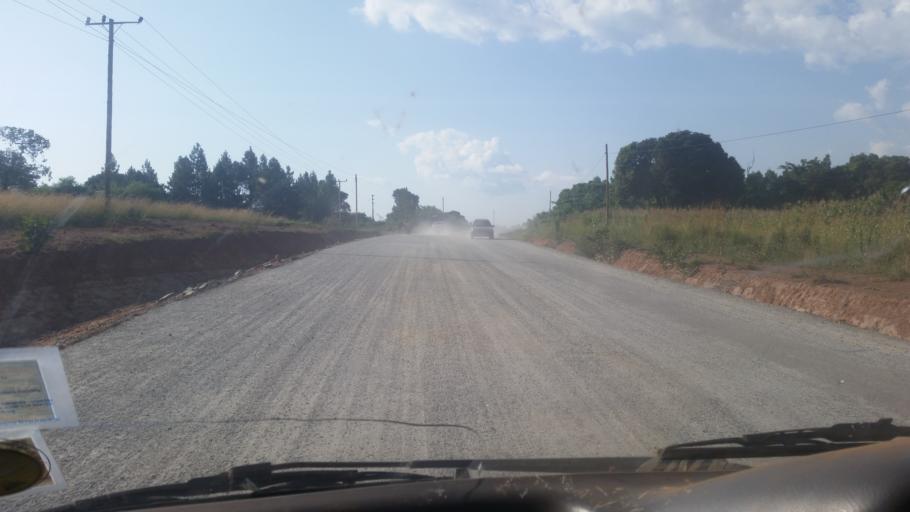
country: UG
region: Western Region
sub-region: Hoima District
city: Hoima
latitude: 1.3933
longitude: 31.3320
